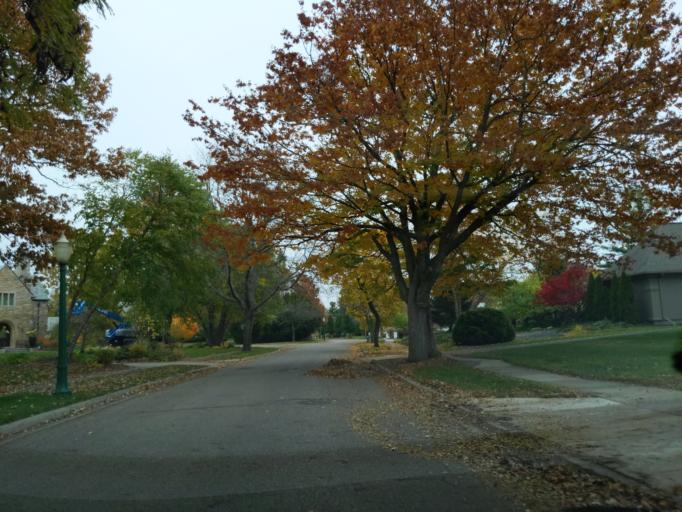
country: US
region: Michigan
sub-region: Ingham County
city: Edgemont Park
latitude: 42.7179
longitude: -84.5850
